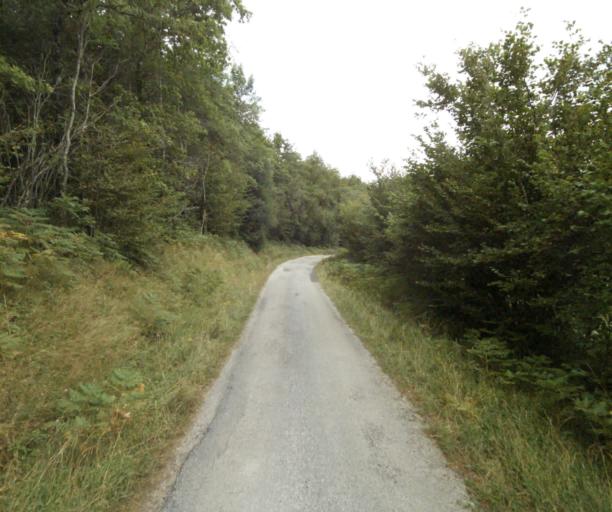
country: FR
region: Midi-Pyrenees
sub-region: Departement du Tarn
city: Soreze
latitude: 43.4268
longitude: 2.0912
